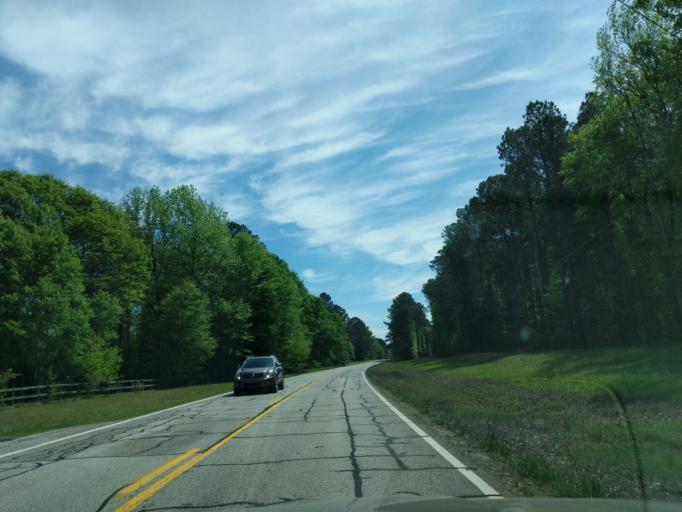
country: US
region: Georgia
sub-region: Columbia County
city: Appling
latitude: 33.6121
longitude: -82.3123
